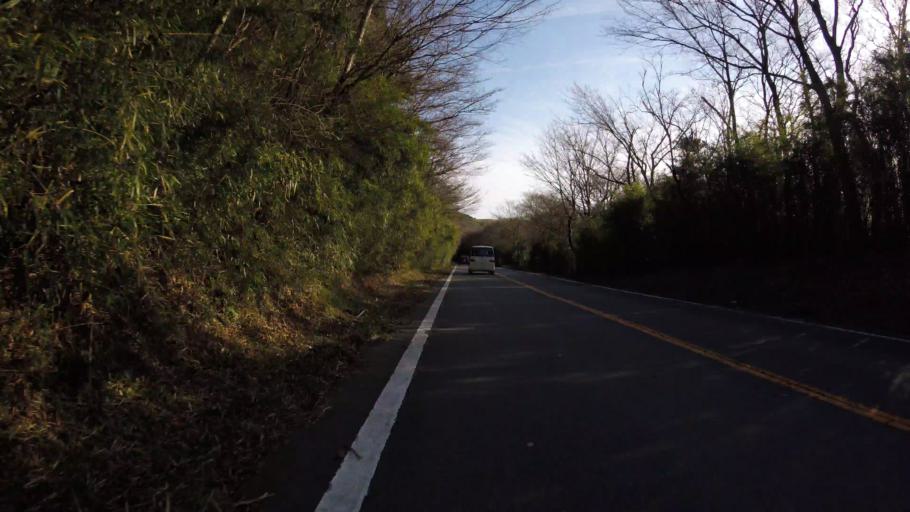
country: JP
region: Kanagawa
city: Hakone
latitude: 35.1600
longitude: 139.0242
